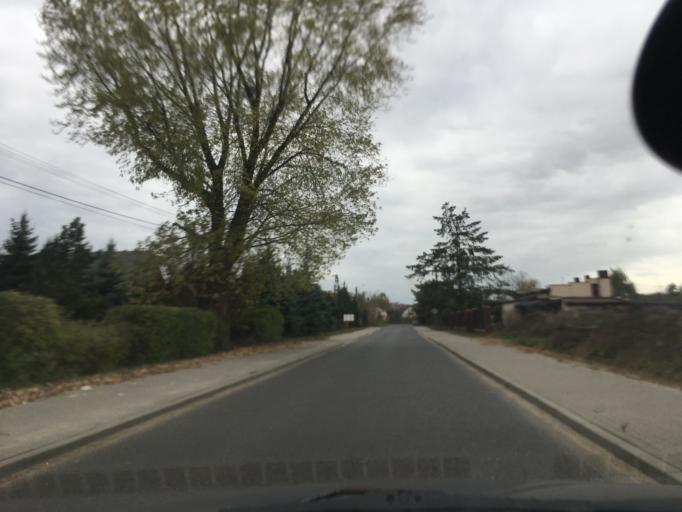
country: PL
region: Lodz Voivodeship
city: Zabia Wola
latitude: 52.0288
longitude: 20.6938
